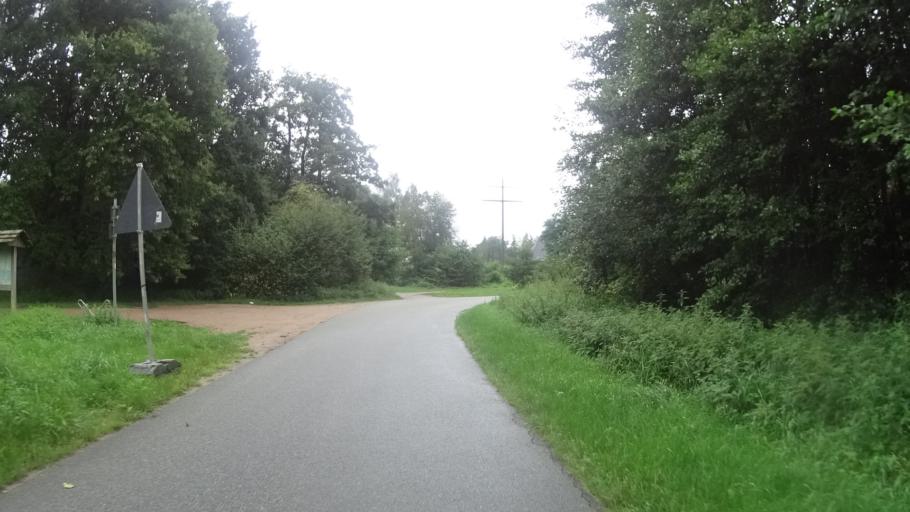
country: DE
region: Schleswig-Holstein
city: Buchen
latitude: 53.4933
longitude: 10.6224
